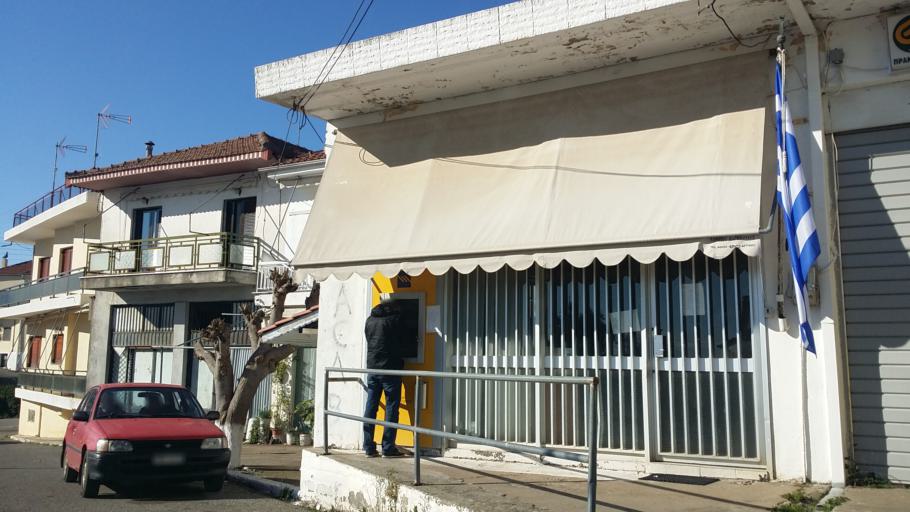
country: GR
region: West Greece
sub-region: Nomos Aitolias kai Akarnanias
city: Fitiai
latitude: 38.6963
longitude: 21.1842
